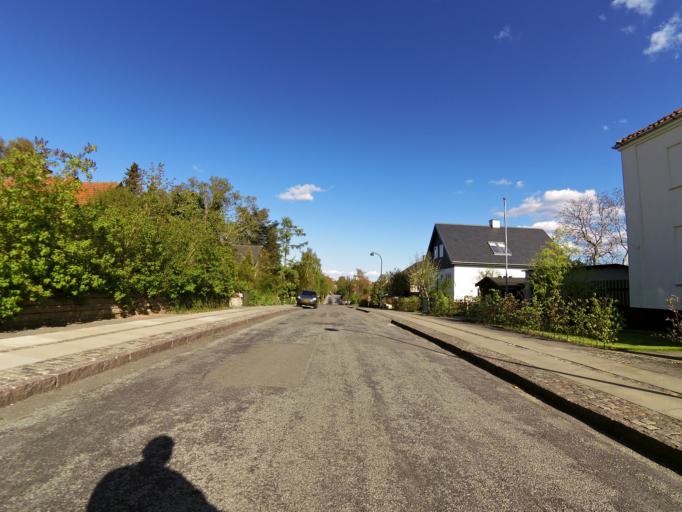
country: DK
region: Capital Region
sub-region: Lyngby-Tarbaek Kommune
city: Kongens Lyngby
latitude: 55.7331
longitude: 12.5272
